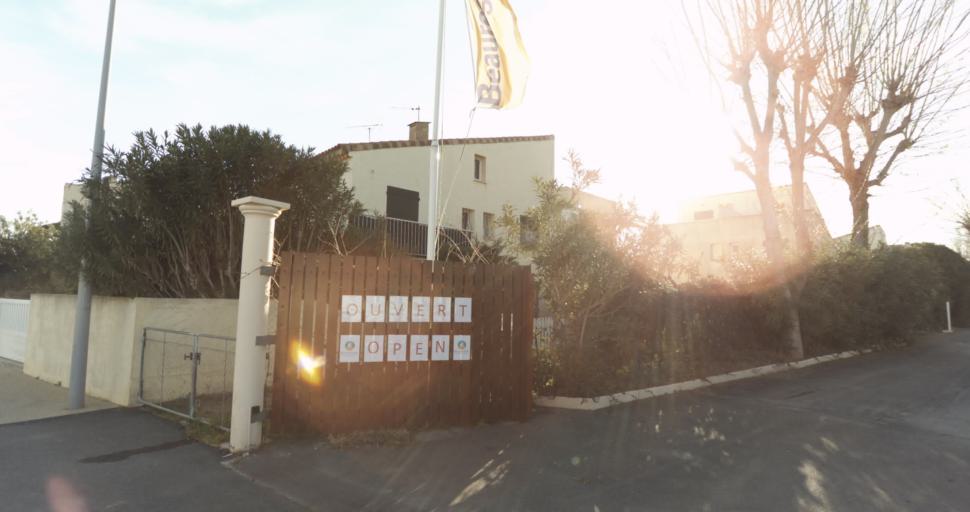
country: FR
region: Languedoc-Roussillon
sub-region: Departement de l'Herault
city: Marseillan
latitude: 43.3150
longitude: 3.5489
